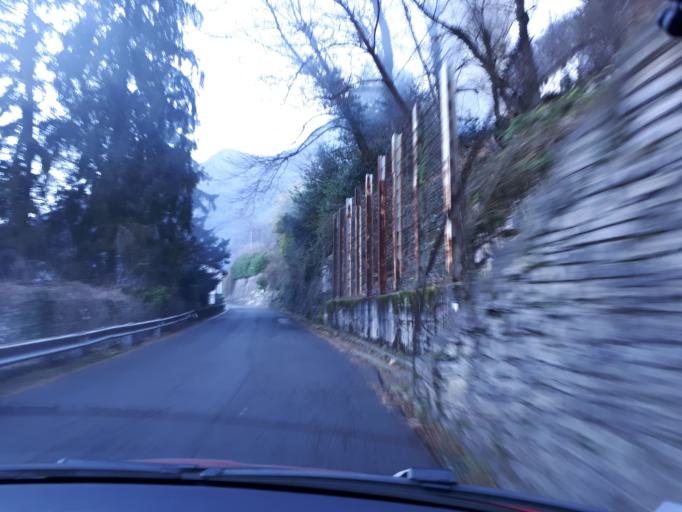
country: IT
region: Lombardy
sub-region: Provincia di Como
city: Faggeto Lario
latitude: 45.8658
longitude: 9.1540
